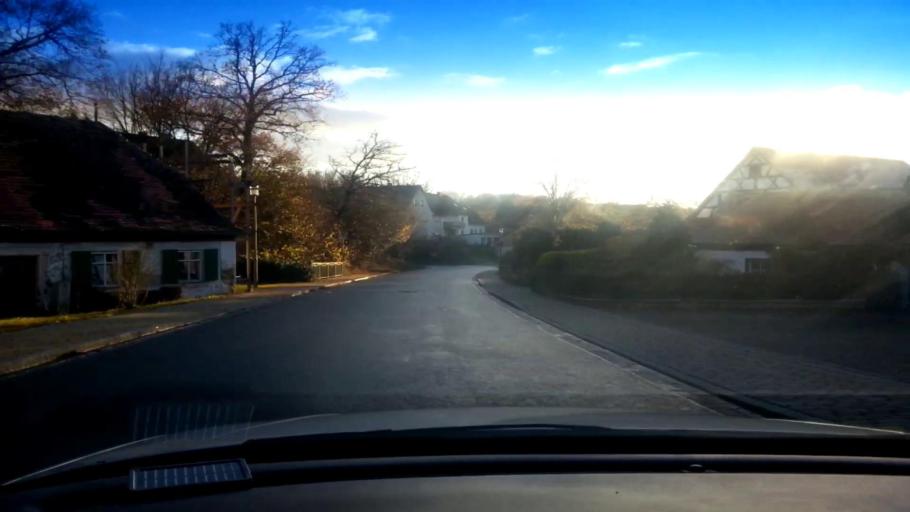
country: DE
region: Bavaria
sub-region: Upper Franconia
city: Buttenheim
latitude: 49.8243
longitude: 11.0275
